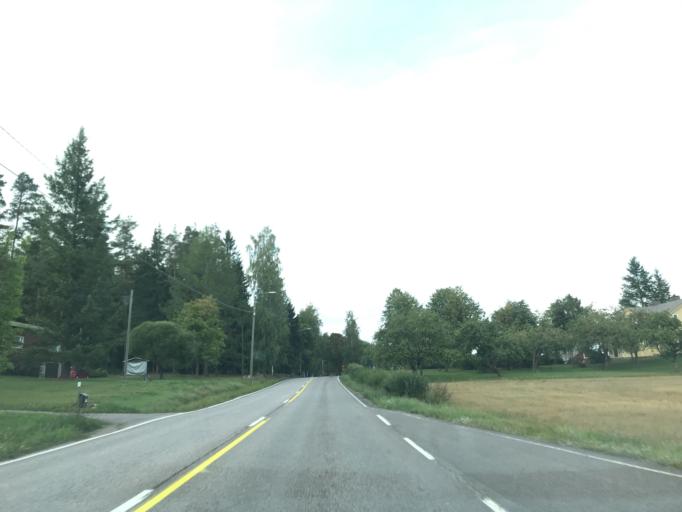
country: FI
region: Uusimaa
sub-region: Helsinki
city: Kirkkonummi
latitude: 60.2349
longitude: 24.4589
